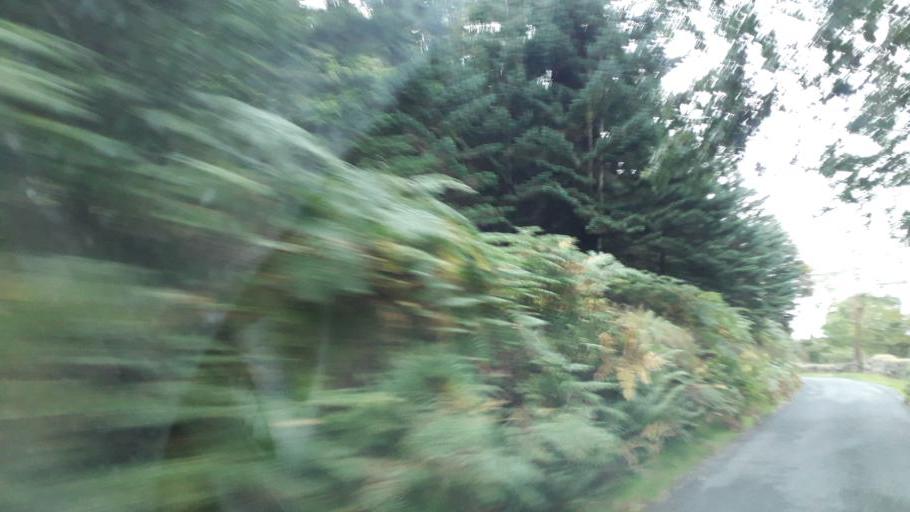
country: IE
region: Leinster
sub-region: Wicklow
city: Enniskerry
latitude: 53.1712
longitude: -6.2406
